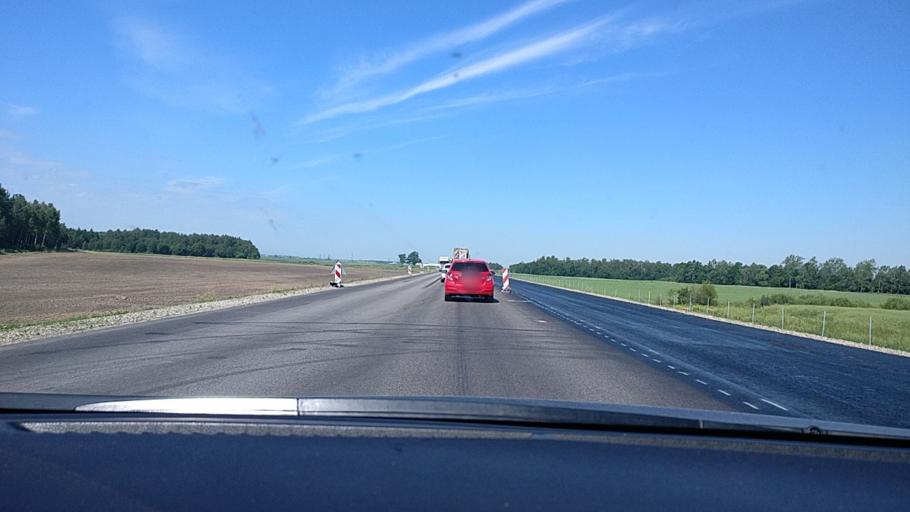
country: LT
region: Panevezys
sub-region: Panevezys City
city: Panevezys
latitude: 55.6767
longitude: 24.3193
